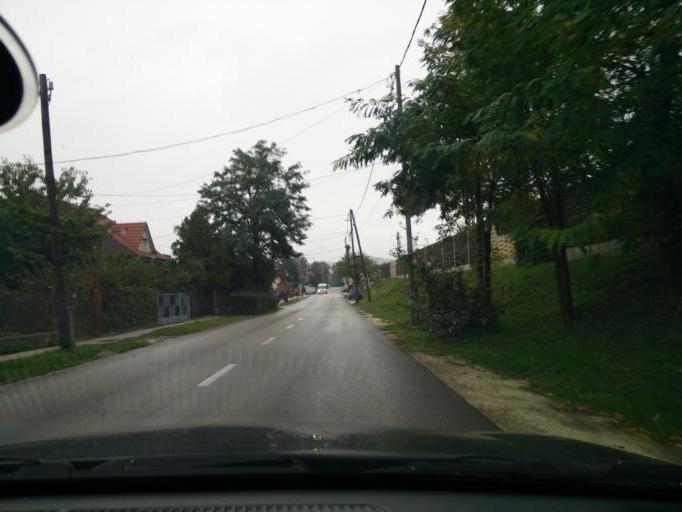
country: HU
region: Komarom-Esztergom
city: Tatabanya
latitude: 47.5635
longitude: 18.4224
